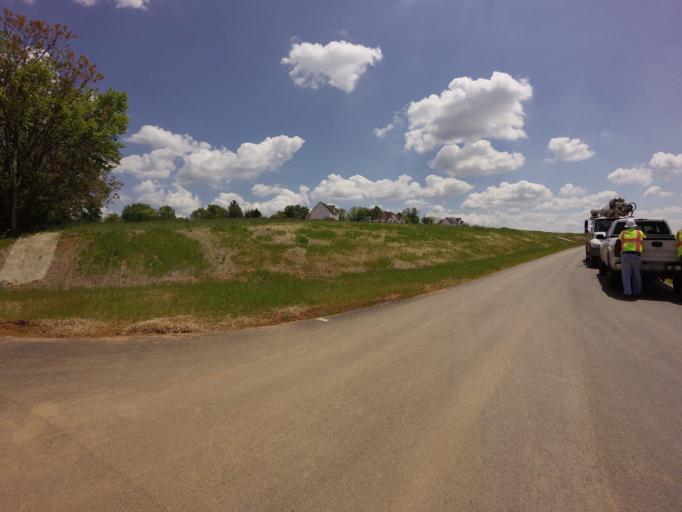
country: US
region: Maryland
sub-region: Frederick County
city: Green Valley
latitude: 39.2940
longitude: -77.3045
